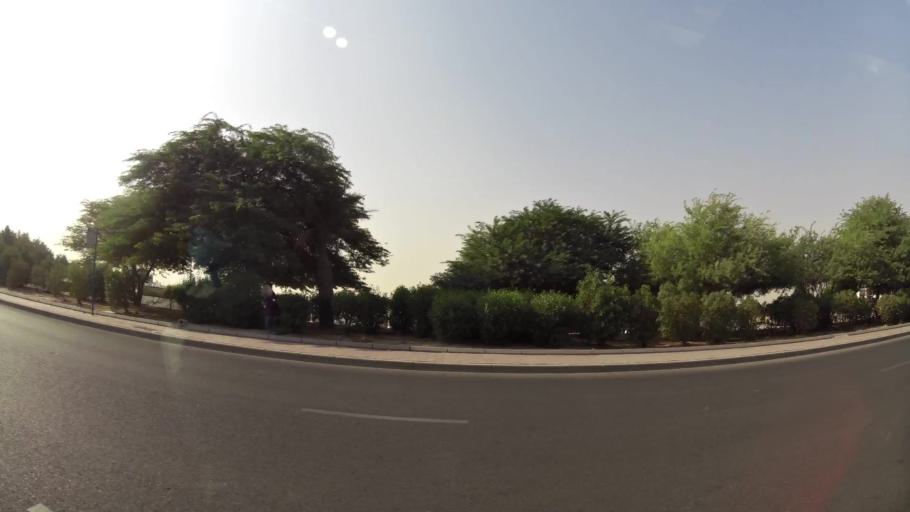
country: KW
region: Al Asimah
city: Ar Rabiyah
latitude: 29.2806
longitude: 47.8365
